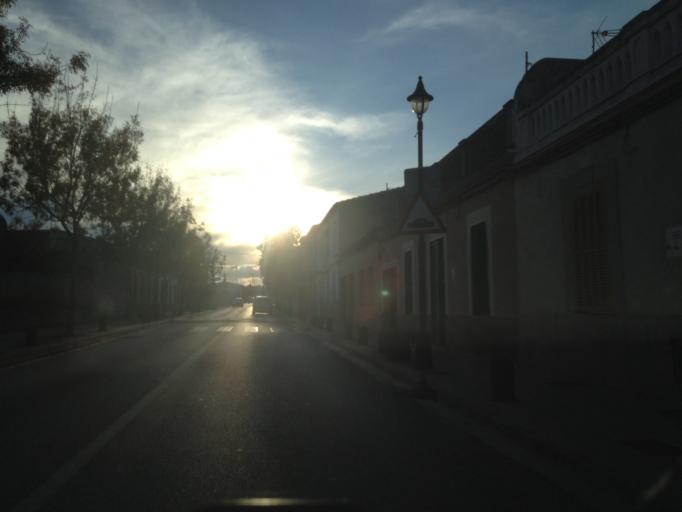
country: ES
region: Balearic Islands
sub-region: Illes Balears
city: Santa Maria del Cami
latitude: 39.6494
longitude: 2.7698
